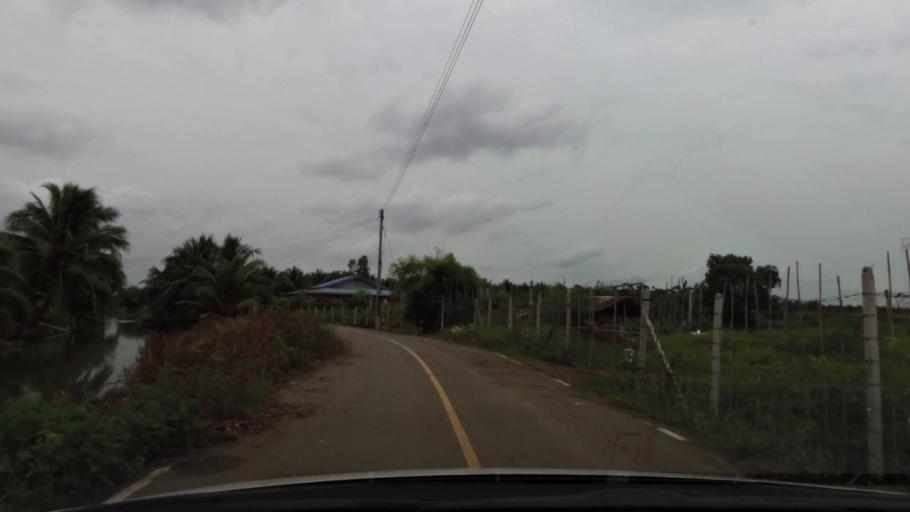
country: TH
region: Samut Sakhon
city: Ban Phaeo
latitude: 13.6105
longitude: 100.0329
